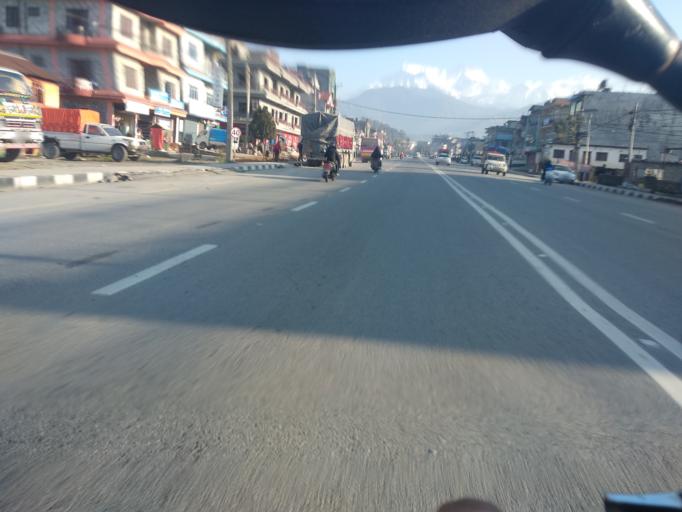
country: NP
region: Western Region
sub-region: Gandaki Zone
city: Pokhara
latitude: 28.2205
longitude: 83.9778
